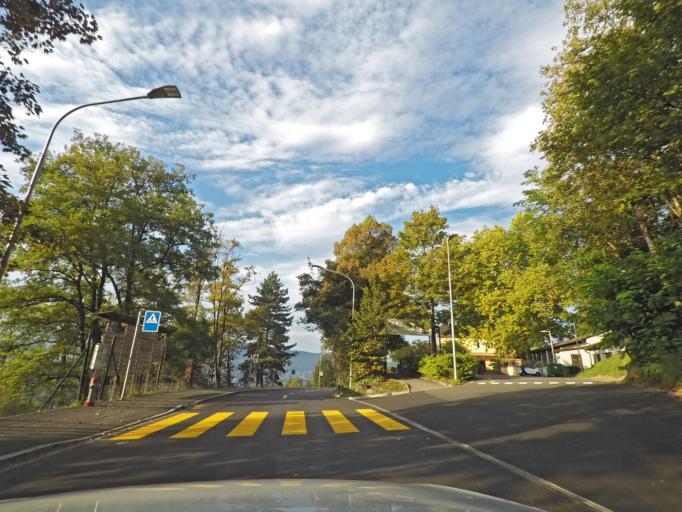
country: CH
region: Zurich
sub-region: Bezirk Zuerich
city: Zuerich (Kreis 10) / Wipkingen
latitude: 47.4005
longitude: 8.5168
